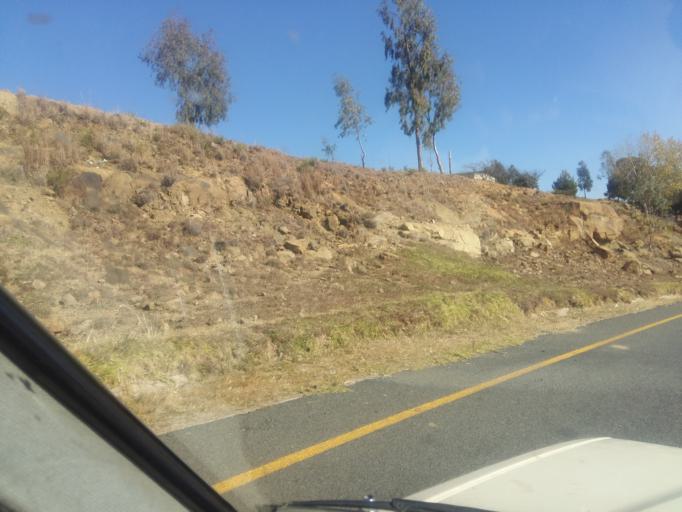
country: LS
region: Mafeteng
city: Mafeteng
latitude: -29.6810
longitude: 27.2790
